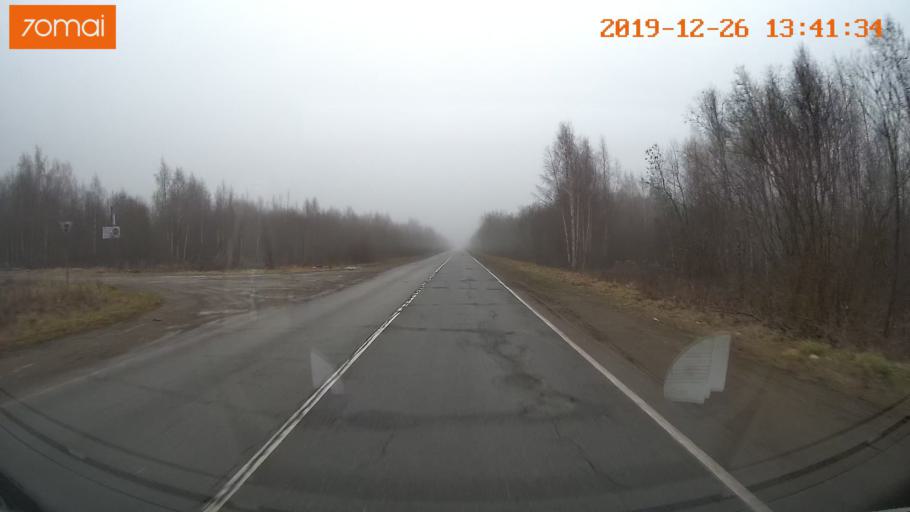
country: RU
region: Vologda
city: Sheksna
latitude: 58.7302
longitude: 38.4514
